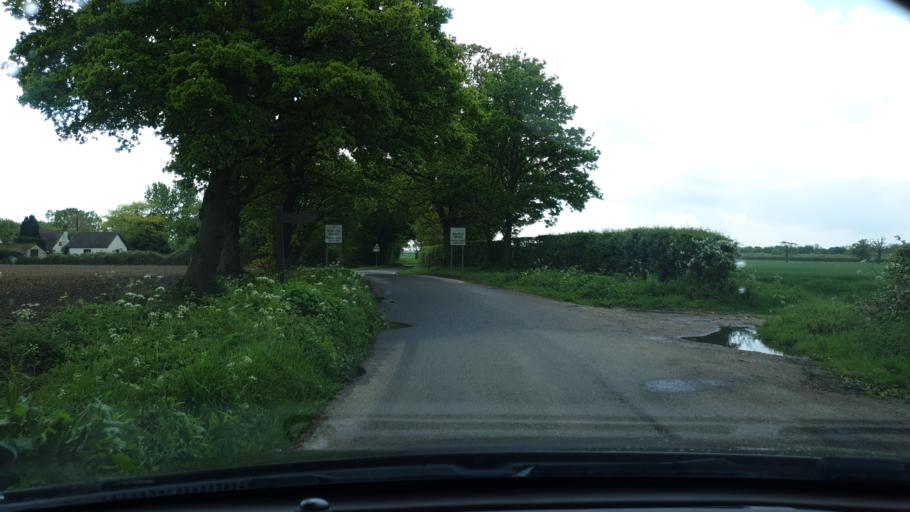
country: GB
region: England
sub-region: Essex
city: Great Bentley
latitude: 51.8801
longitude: 1.0549
